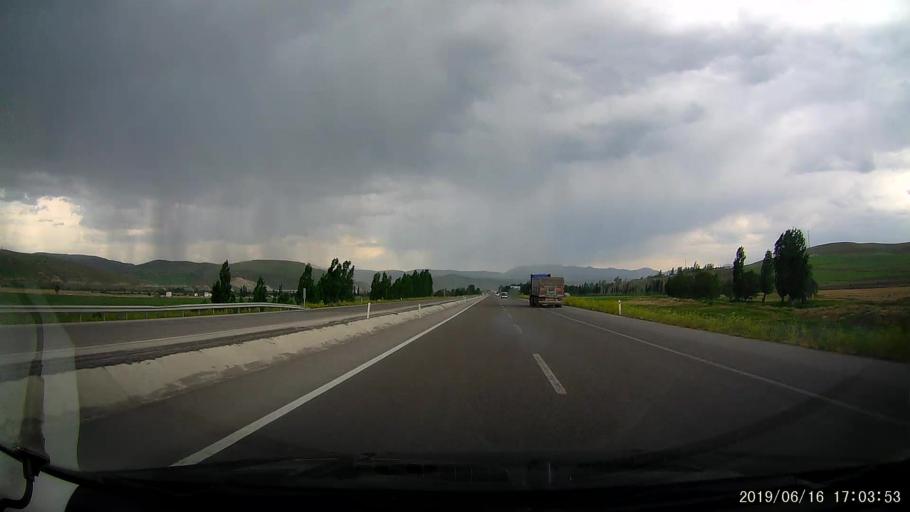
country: TR
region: Erzurum
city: Askale
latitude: 39.9320
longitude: 40.7215
